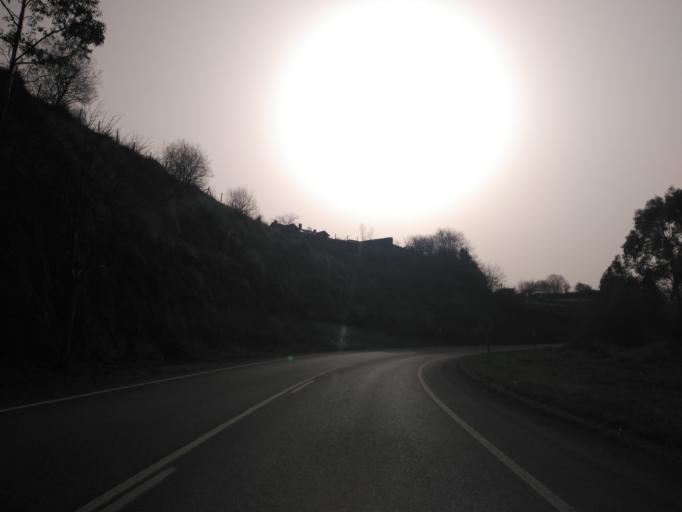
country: ES
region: Cantabria
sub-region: Provincia de Cantabria
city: Cabezon de la Sal
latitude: 43.3399
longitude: -4.2719
